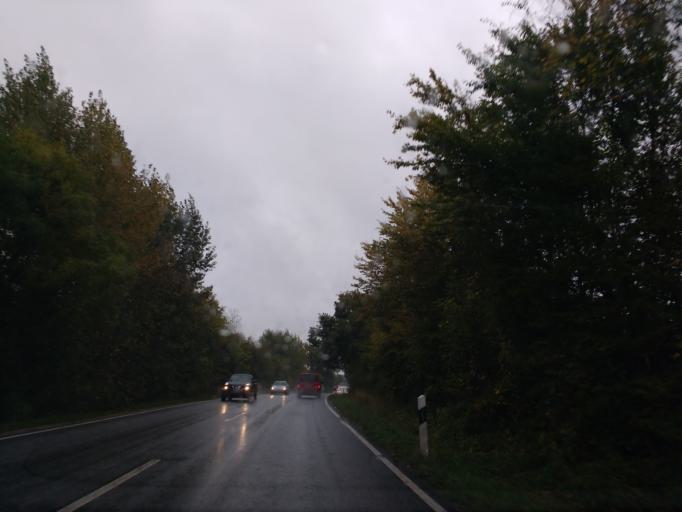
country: DE
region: Schleswig-Holstein
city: Eutin
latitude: 54.1109
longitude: 10.6600
